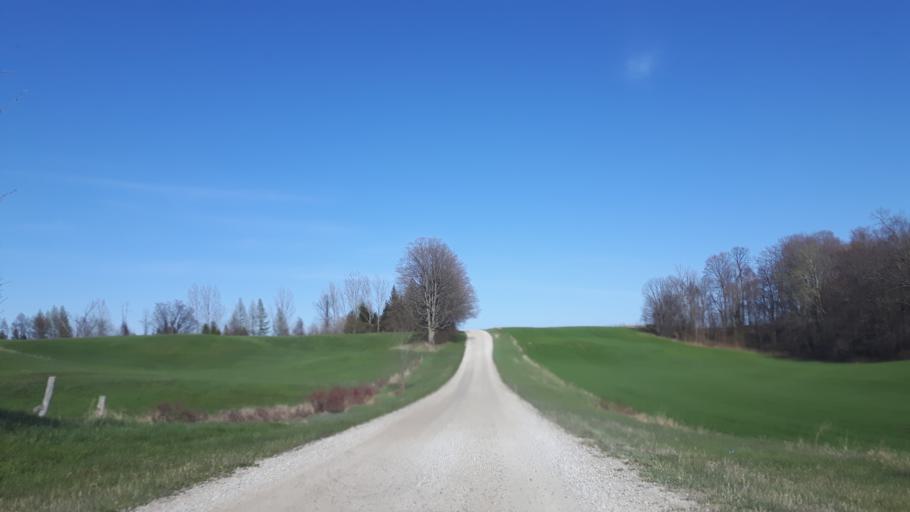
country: CA
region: Ontario
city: Goderich
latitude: 43.6613
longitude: -81.6774
